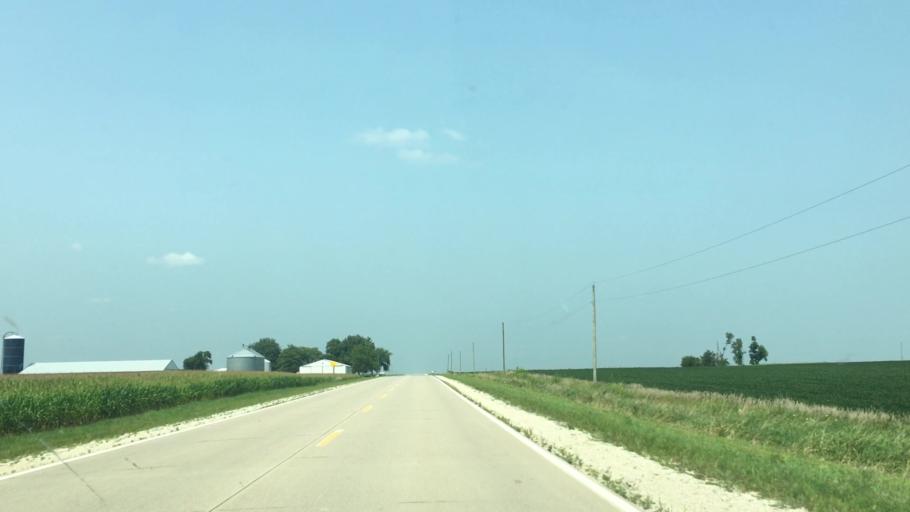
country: US
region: Iowa
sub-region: Fayette County
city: Fayette
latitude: 42.7412
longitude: -91.8040
